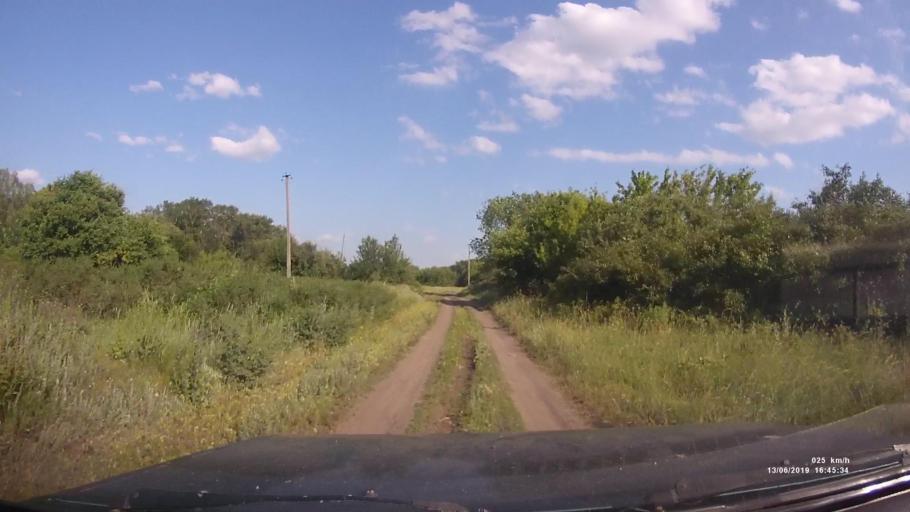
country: RU
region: Rostov
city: Kazanskaya
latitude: 49.9475
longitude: 41.4234
